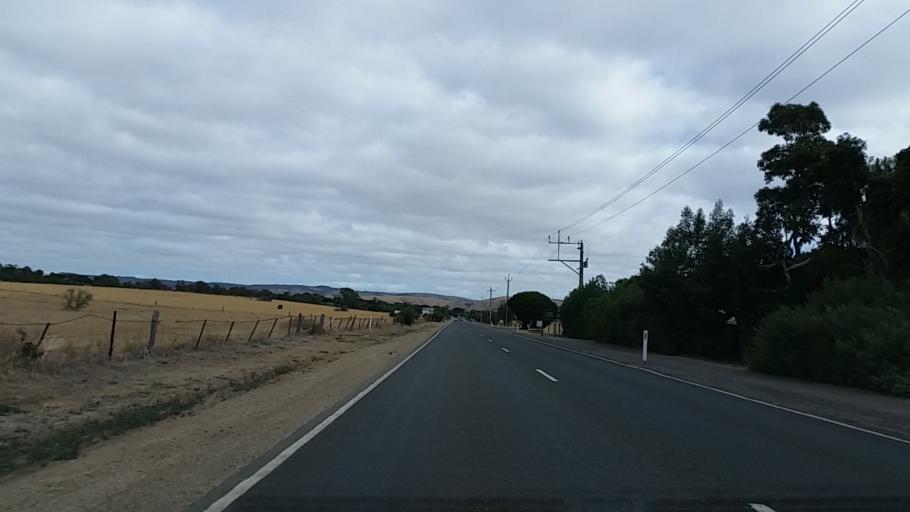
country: AU
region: South Australia
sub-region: Yankalilla
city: Normanville
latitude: -35.4362
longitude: 138.3205
